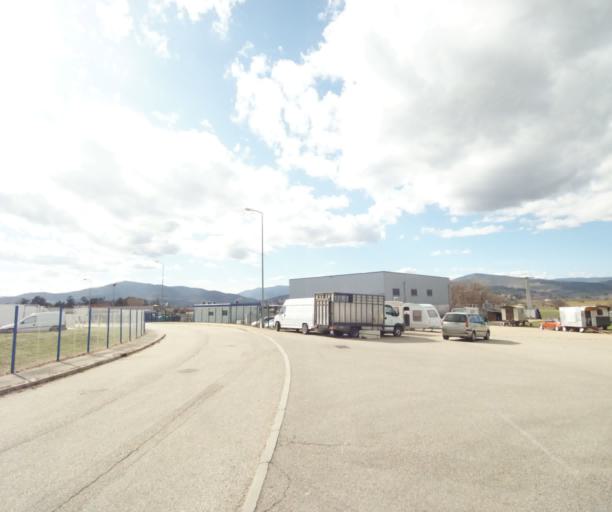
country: FR
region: Rhone-Alpes
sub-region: Departement de l'Ardeche
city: Davezieux
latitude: 45.2595
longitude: 4.6931
